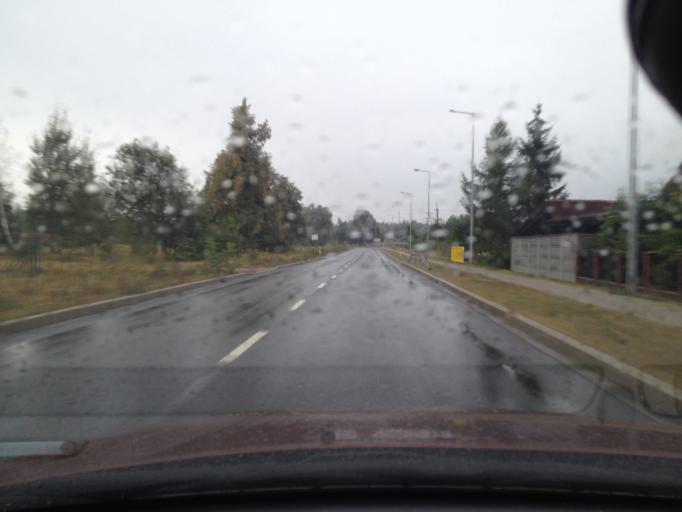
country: PL
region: Lubusz
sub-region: Powiat zaganski
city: Ilowa
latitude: 51.4926
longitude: 15.1929
